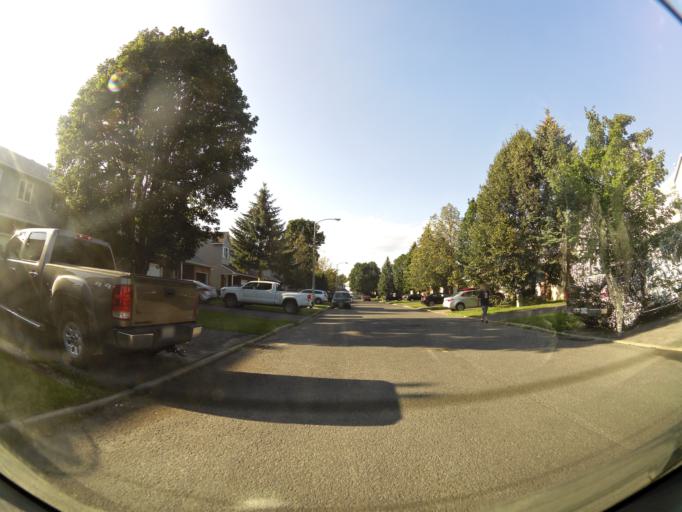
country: CA
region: Ontario
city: Clarence-Rockland
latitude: 45.4788
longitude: -75.4897
